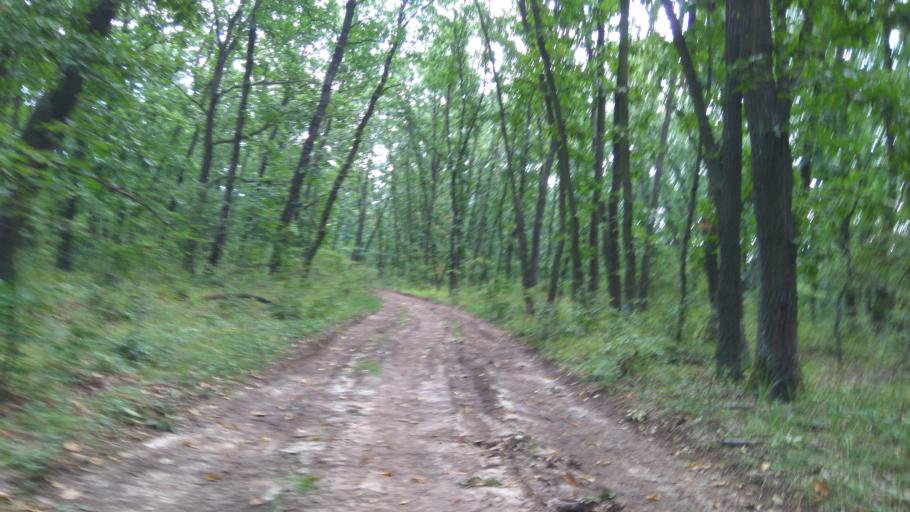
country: SK
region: Nitriansky
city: Sahy
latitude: 48.0144
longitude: 18.9330
